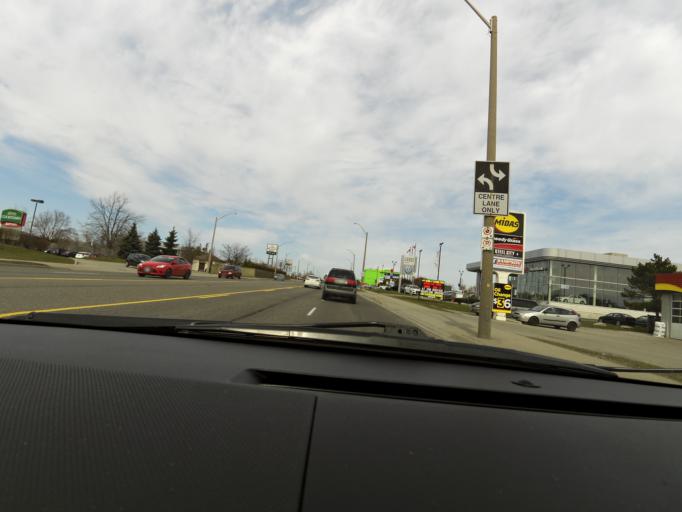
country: CA
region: Ontario
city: Hamilton
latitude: 43.2145
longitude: -79.8876
